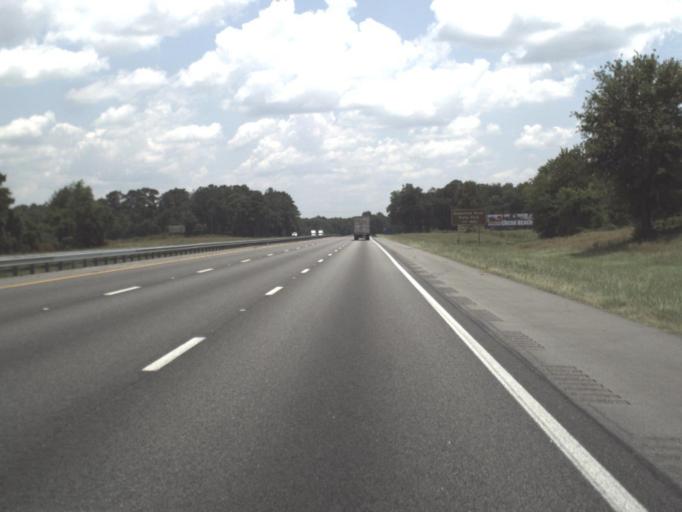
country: US
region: Florida
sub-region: Hamilton County
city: Jasper
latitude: 30.5305
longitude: -83.0689
